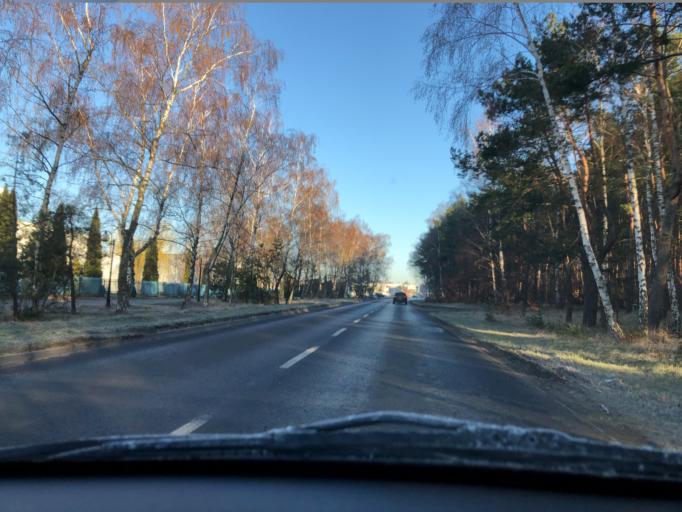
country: PL
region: Greater Poland Voivodeship
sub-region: Powiat poznanski
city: Plewiska
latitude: 52.3951
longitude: 16.8057
